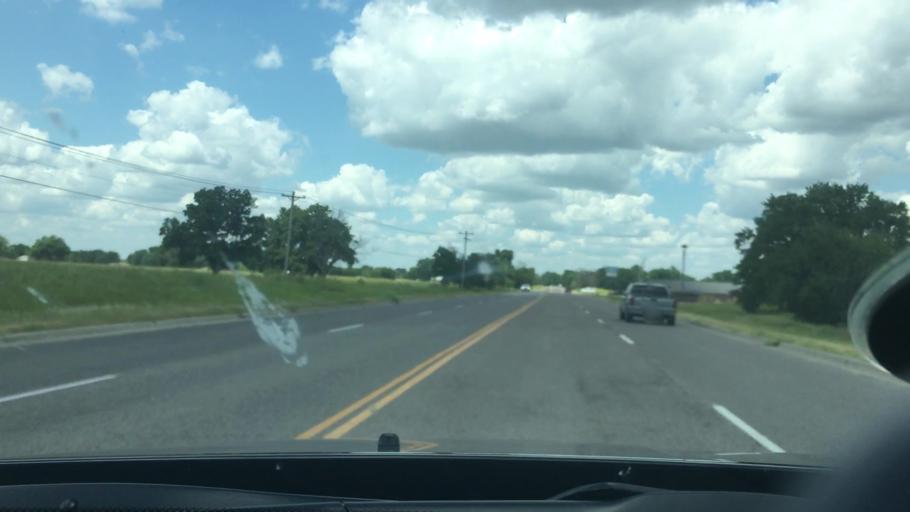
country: US
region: Oklahoma
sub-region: Murray County
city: Davis
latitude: 34.4650
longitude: -97.1307
